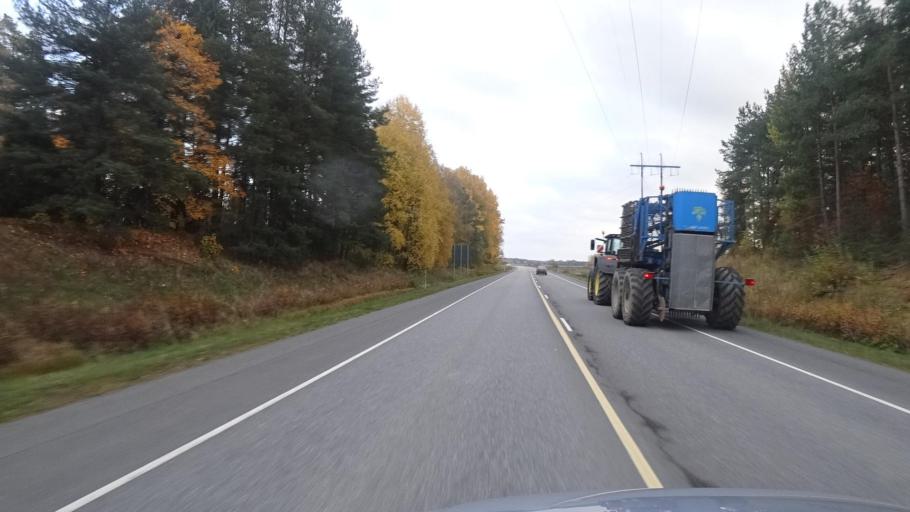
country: FI
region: Satakunta
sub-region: Rauma
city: Saekylae
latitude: 61.0373
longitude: 22.3876
